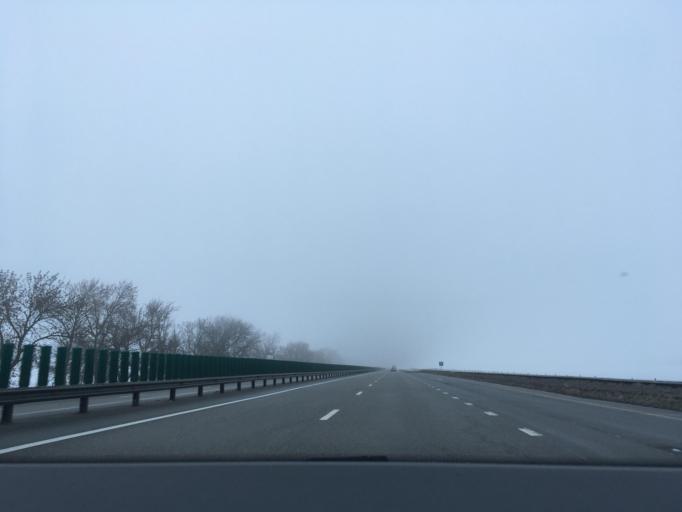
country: RU
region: Krasnodarskiy
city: Kushchevskaya
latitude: 46.6213
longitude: 39.6585
